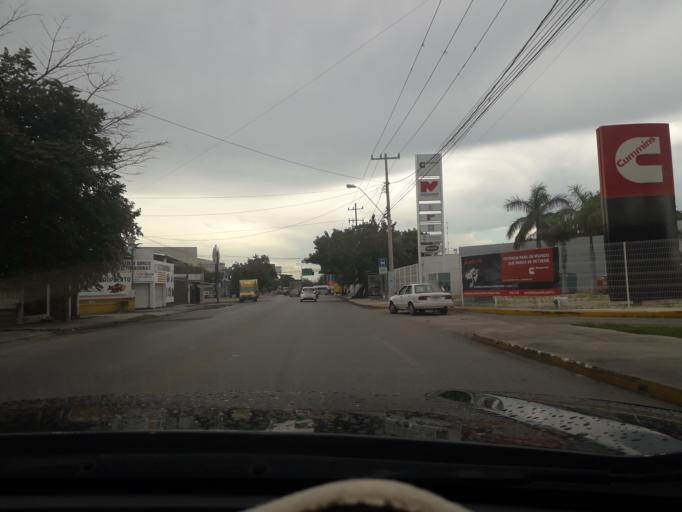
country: MX
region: Yucatan
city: Merida
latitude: 20.9502
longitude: -89.6499
